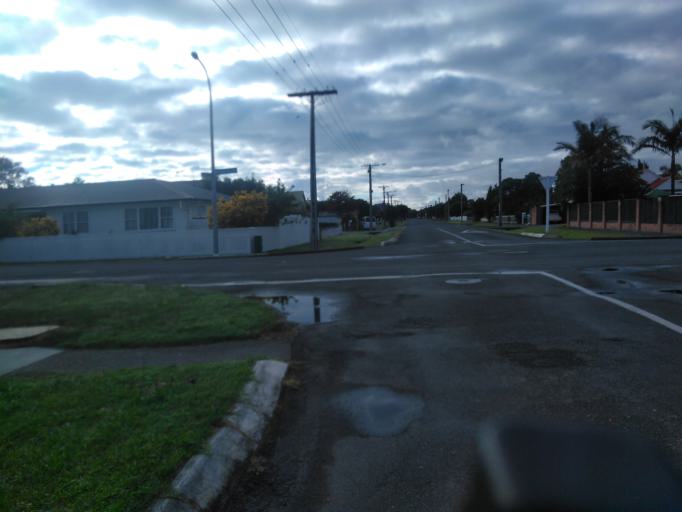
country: NZ
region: Gisborne
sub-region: Gisborne District
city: Gisborne
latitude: -38.6541
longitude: 178.0261
